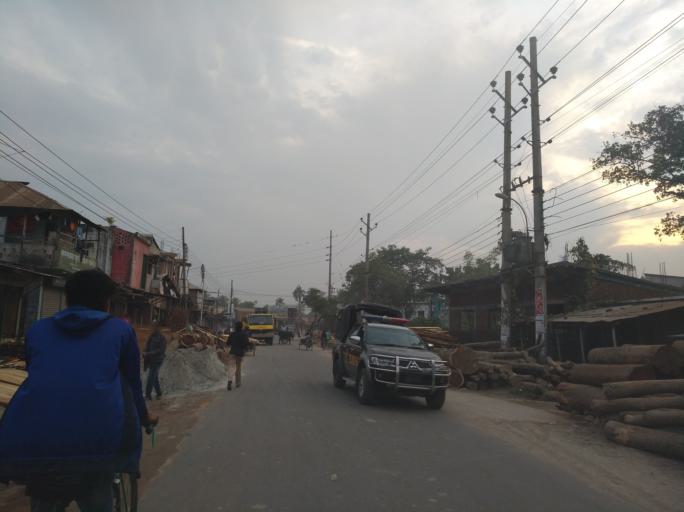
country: BD
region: Khulna
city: Khulna
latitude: 22.8462
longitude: 89.5412
